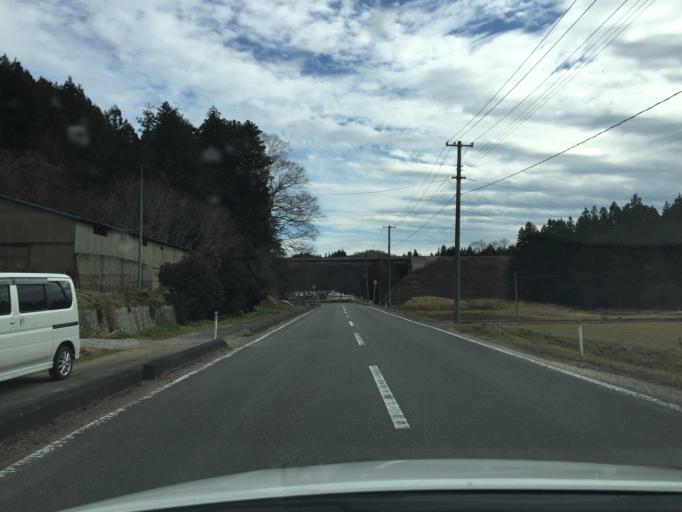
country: JP
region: Fukushima
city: Funehikimachi-funehiki
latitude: 37.2874
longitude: 140.6004
